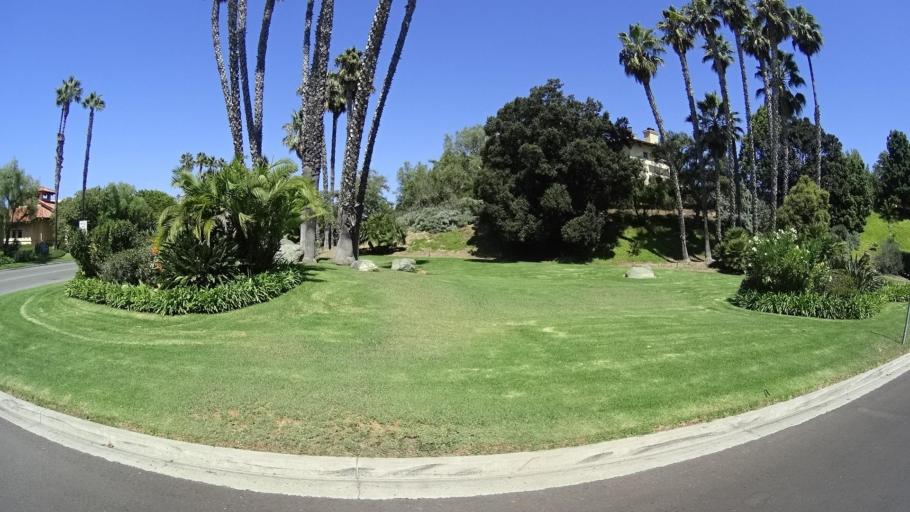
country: US
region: California
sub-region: San Diego County
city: Fairbanks Ranch
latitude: 32.9898
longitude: -117.1954
